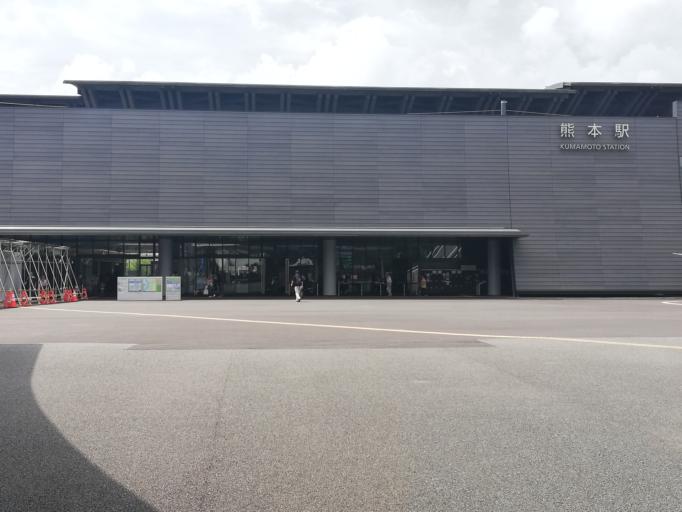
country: JP
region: Kumamoto
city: Kumamoto
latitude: 32.7888
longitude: 130.6891
